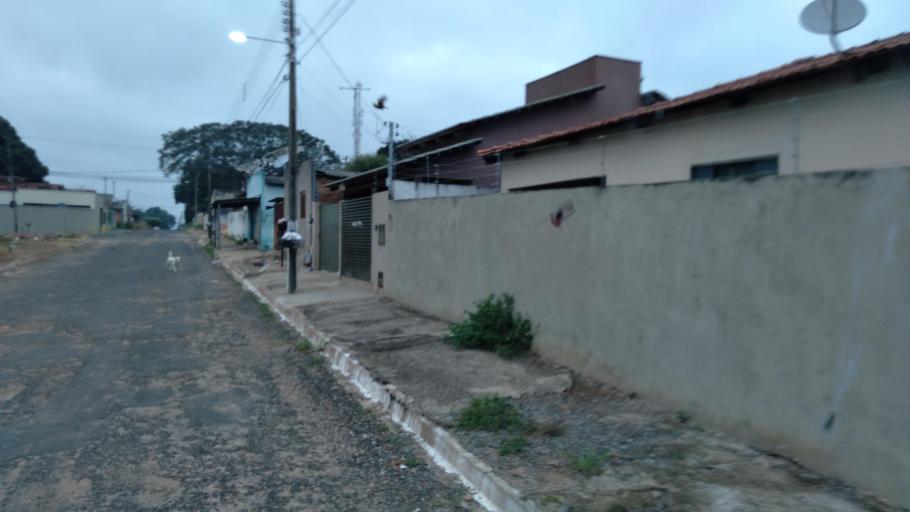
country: BR
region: Goias
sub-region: Mineiros
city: Mineiros
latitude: -17.5804
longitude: -52.5485
